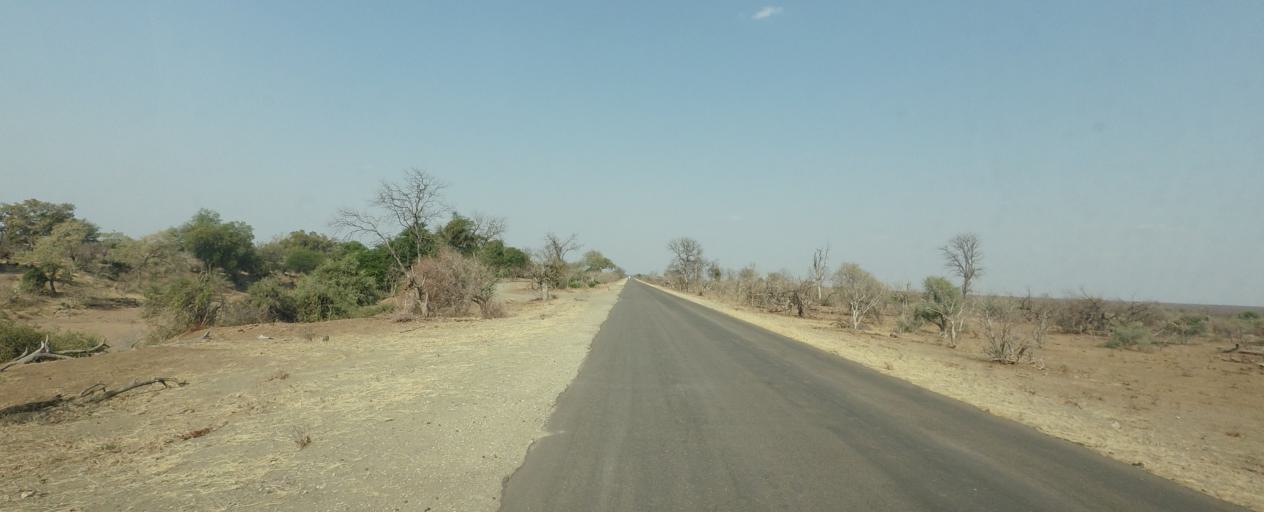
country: ZA
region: Limpopo
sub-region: Mopani District Municipality
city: Giyani
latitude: -23.0969
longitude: 31.3963
